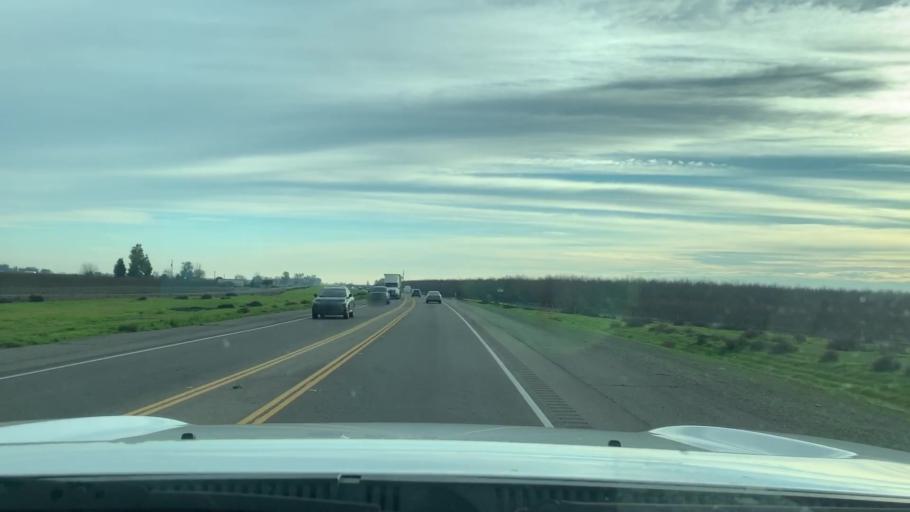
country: US
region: California
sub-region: Fresno County
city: Caruthers
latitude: 36.4854
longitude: -119.7914
